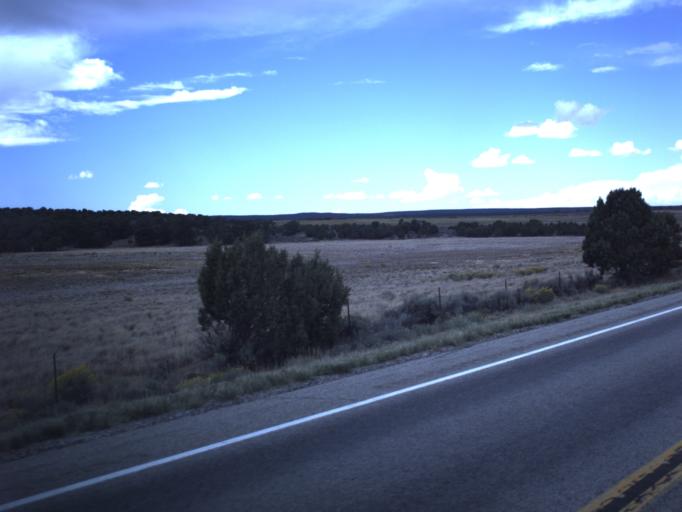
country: US
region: Utah
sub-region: San Juan County
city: Monticello
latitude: 37.9172
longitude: -109.3460
